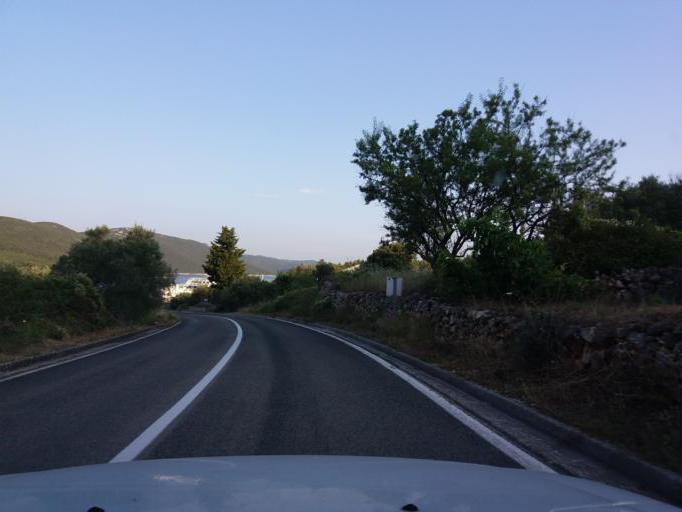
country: HR
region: Zadarska
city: Ugljan
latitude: 44.0834
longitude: 15.0001
